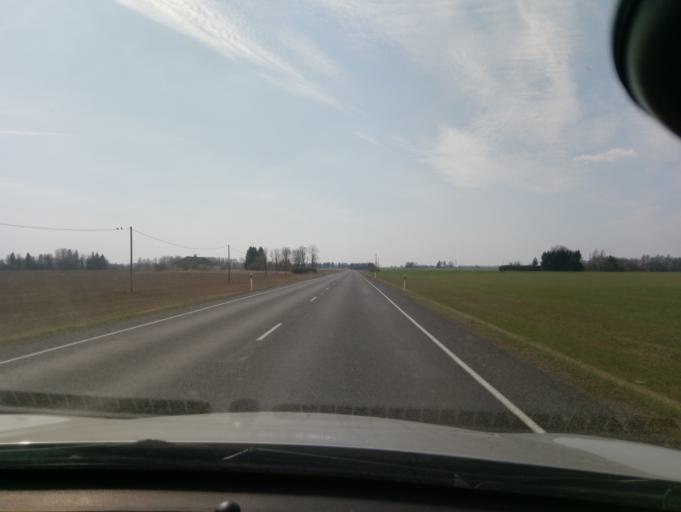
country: EE
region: Viljandimaa
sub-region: Vohma linn
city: Vohma
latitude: 58.6840
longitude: 25.6155
